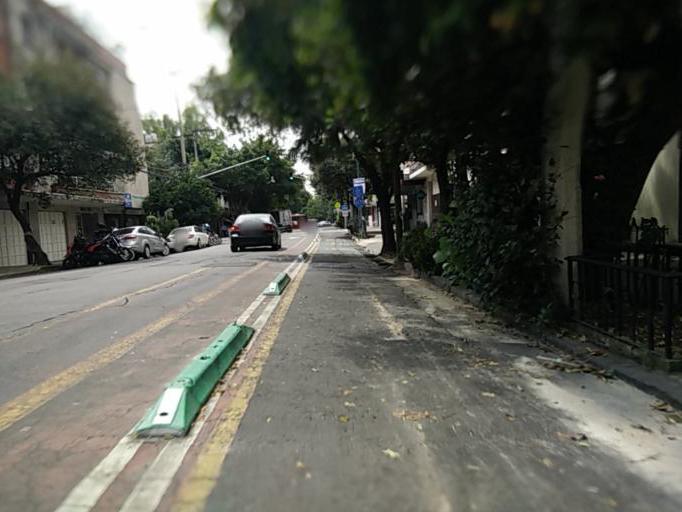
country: MX
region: Mexico City
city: Benito Juarez
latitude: 19.4215
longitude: -99.1669
